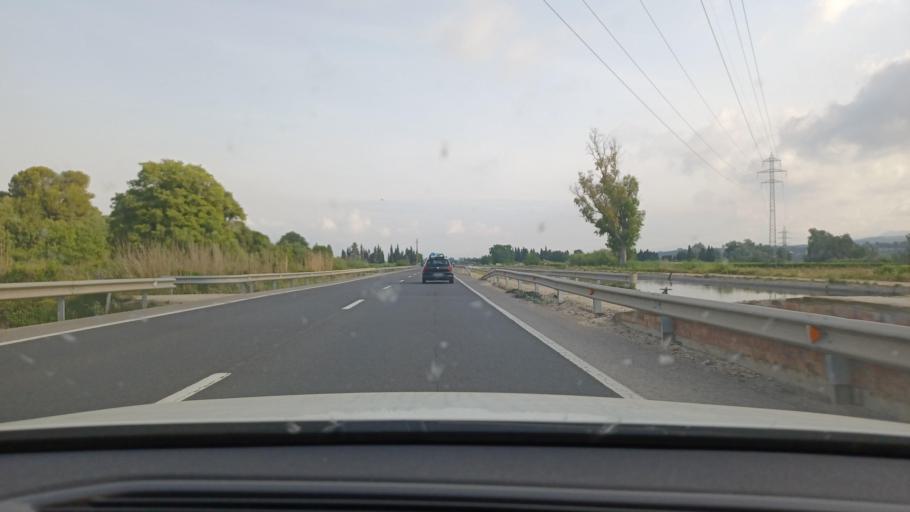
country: ES
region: Catalonia
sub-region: Provincia de Tarragona
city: Masdenverge
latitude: 40.7629
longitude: 0.5334
